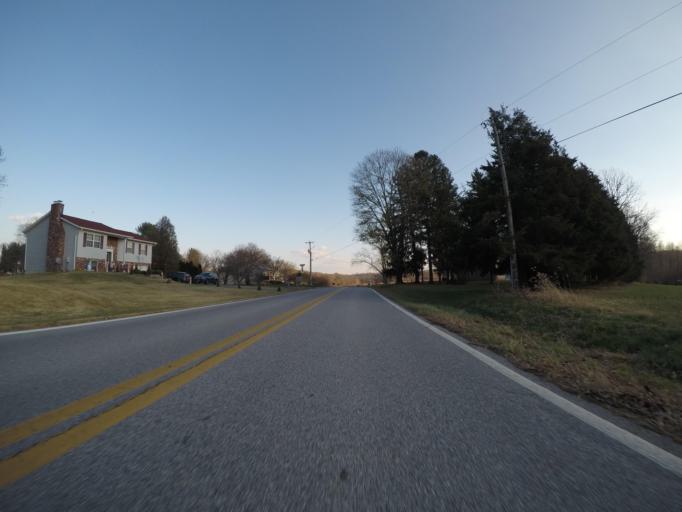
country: US
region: Maryland
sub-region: Carroll County
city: Hampstead
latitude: 39.5736
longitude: -76.9062
